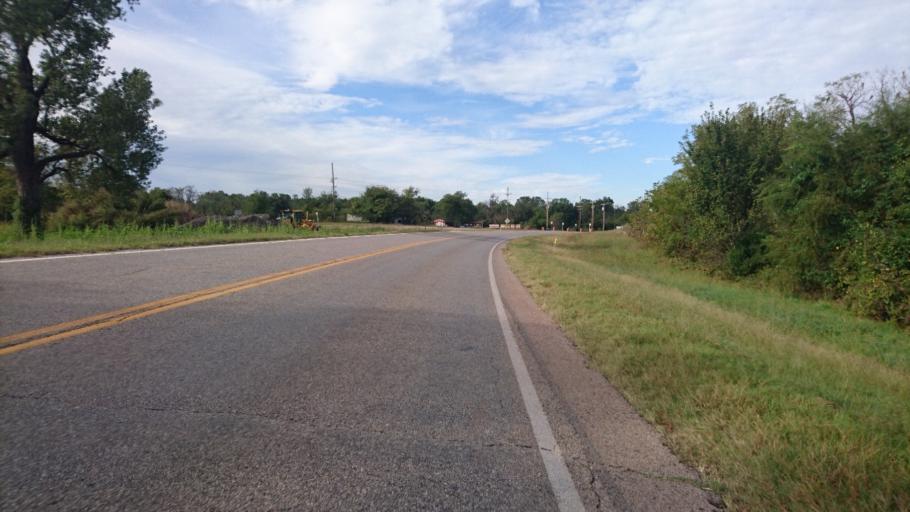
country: US
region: Oklahoma
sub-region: Lincoln County
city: Chandler
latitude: 35.6820
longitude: -97.0028
